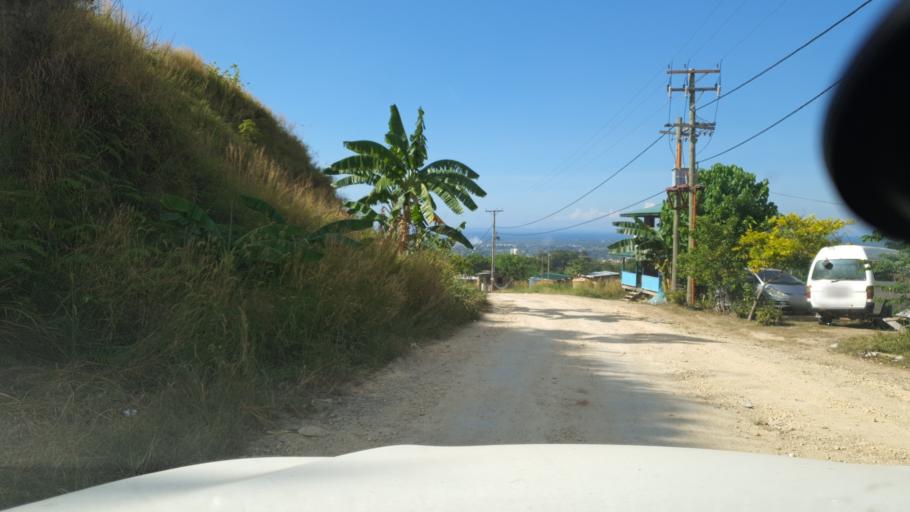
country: SB
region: Guadalcanal
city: Honiara
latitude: -9.4588
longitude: 159.9764
